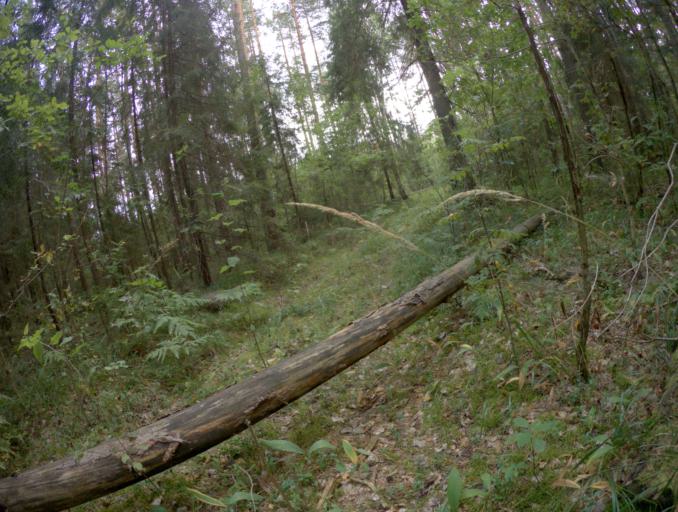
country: RU
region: Vladimir
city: Orgtrud
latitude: 56.1132
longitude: 40.7028
